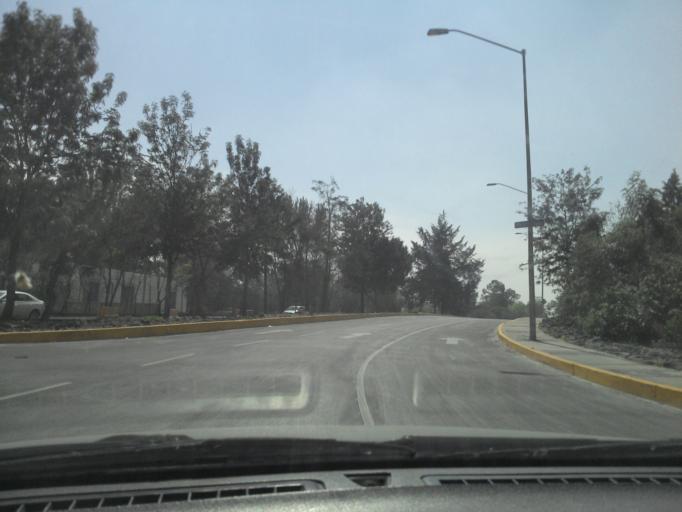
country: MX
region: Mexico City
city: Tlalpan
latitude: 19.3174
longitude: -99.1866
